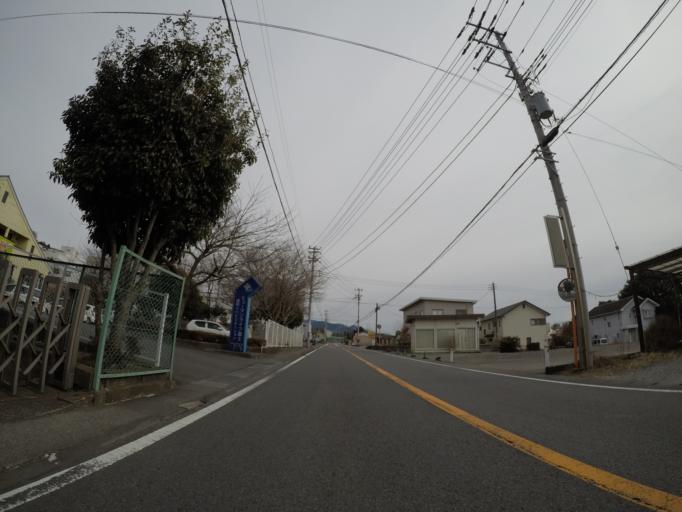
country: JP
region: Shizuoka
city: Fuji
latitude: 35.2151
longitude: 138.6684
